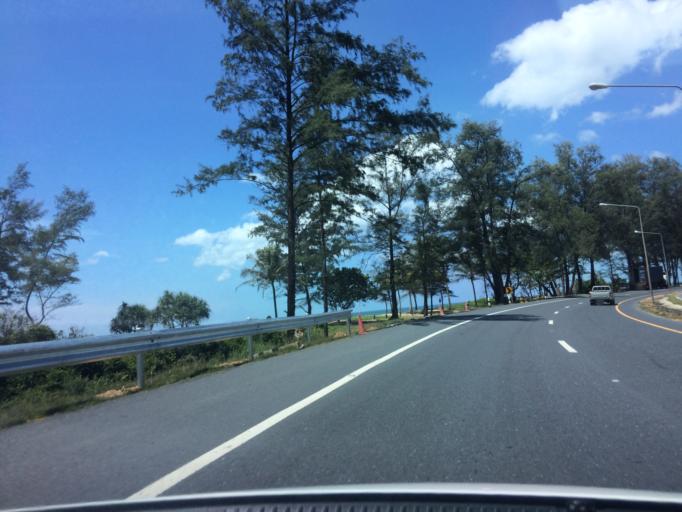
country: TH
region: Phuket
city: Thalang
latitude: 8.1841
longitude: 98.2901
